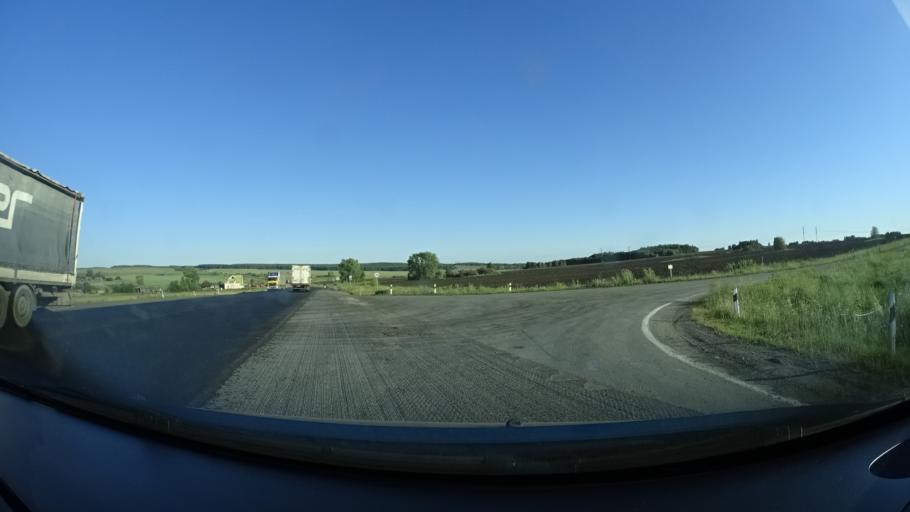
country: RU
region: Sverdlovsk
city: Achit
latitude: 56.8952
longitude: 57.6036
